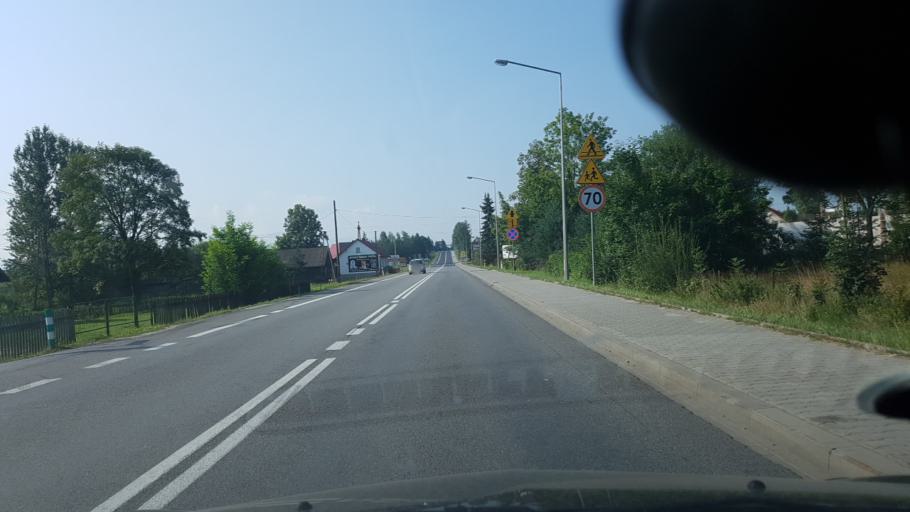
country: PL
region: Lesser Poland Voivodeship
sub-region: Powiat nowotarski
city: Jablonka
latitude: 49.4643
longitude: 19.6913
